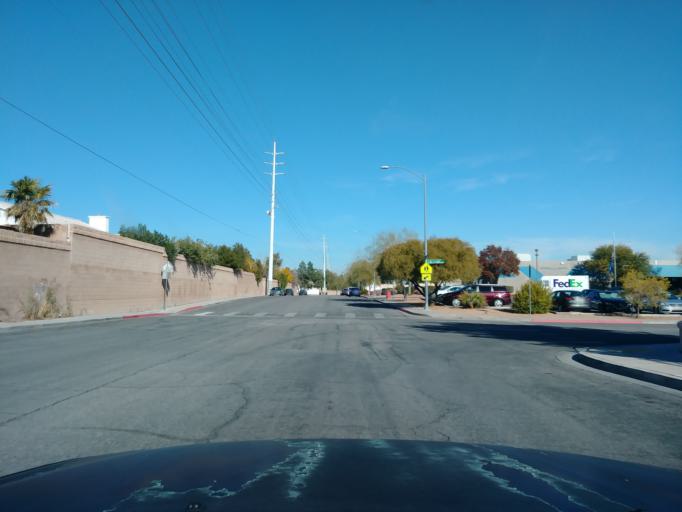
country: US
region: Nevada
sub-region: Clark County
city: Spring Valley
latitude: 36.1494
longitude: -115.2772
